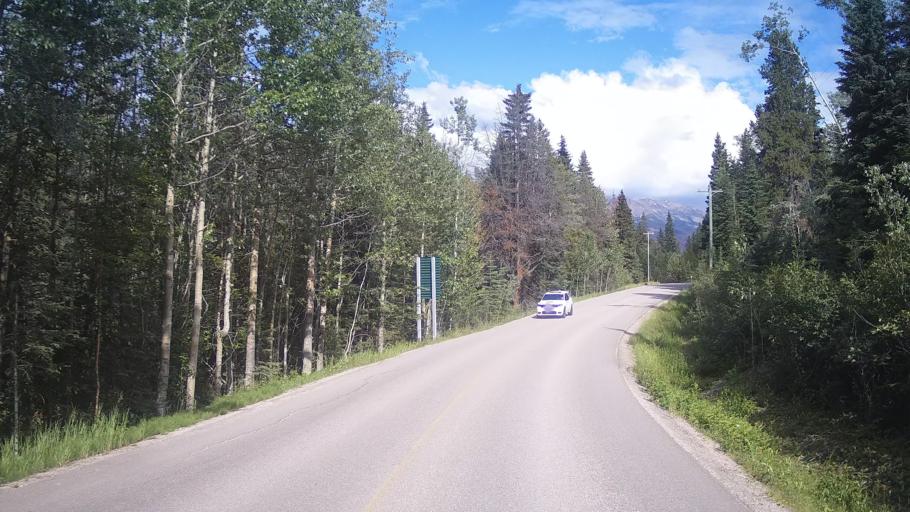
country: CA
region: Alberta
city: Jasper Park Lodge
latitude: 52.8525
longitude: -118.1097
